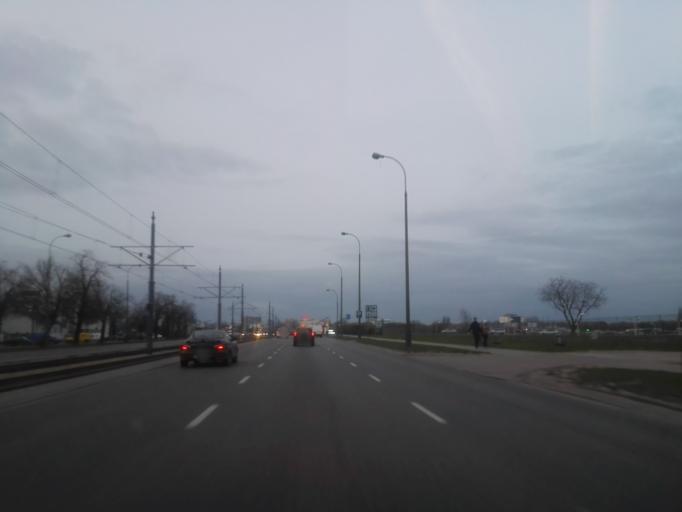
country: PL
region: Masovian Voivodeship
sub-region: Warszawa
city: Wlochy
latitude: 52.1803
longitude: 20.9485
